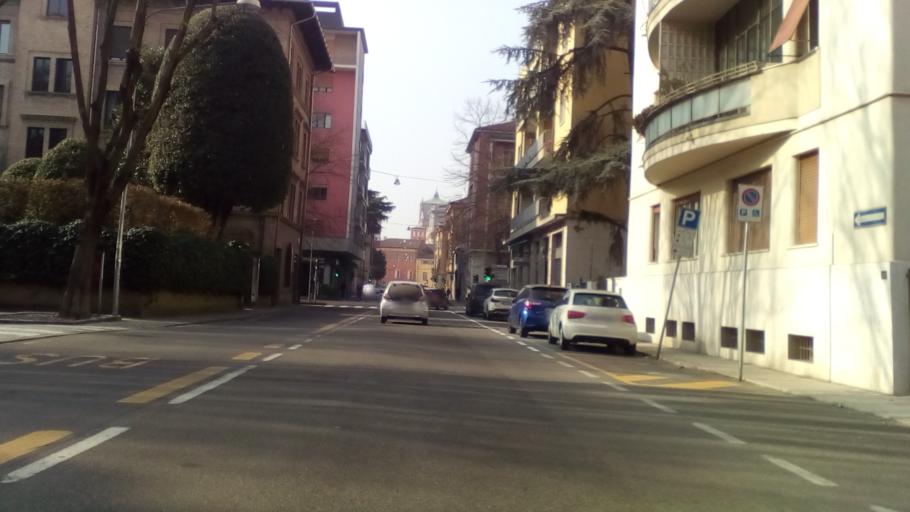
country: IT
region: Emilia-Romagna
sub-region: Provincia di Modena
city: Modena
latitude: 44.6460
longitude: 10.9347
